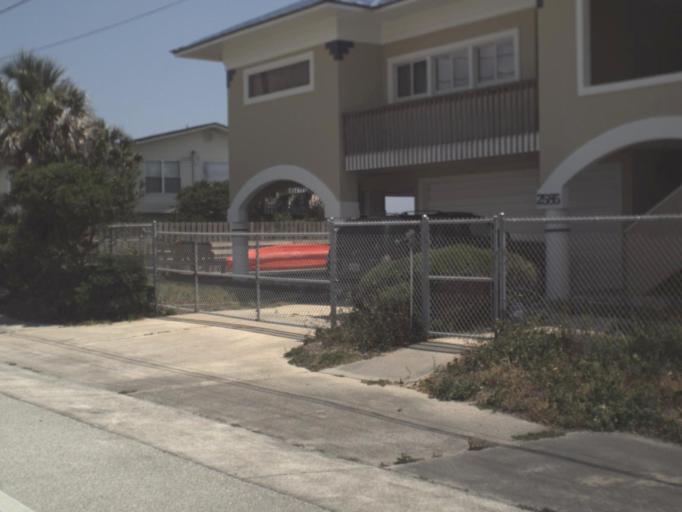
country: US
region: Florida
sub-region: Saint Johns County
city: Villano Beach
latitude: 30.0376
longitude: -81.3271
